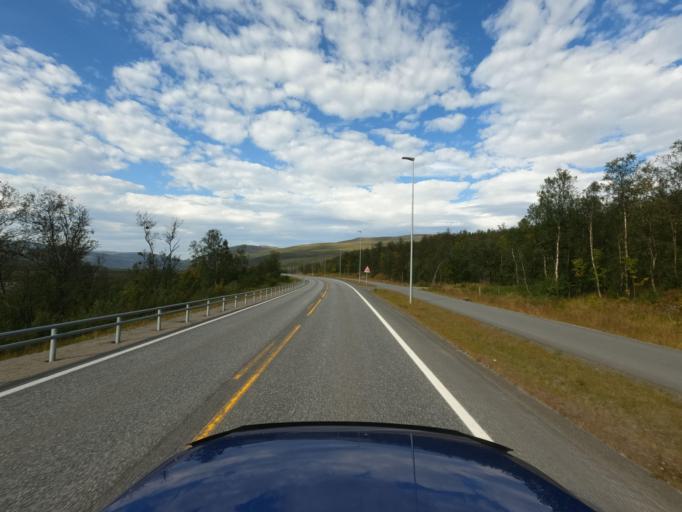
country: NO
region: Finnmark Fylke
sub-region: Kvalsund
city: Kvalsund
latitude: 70.4360
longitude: 24.4888
